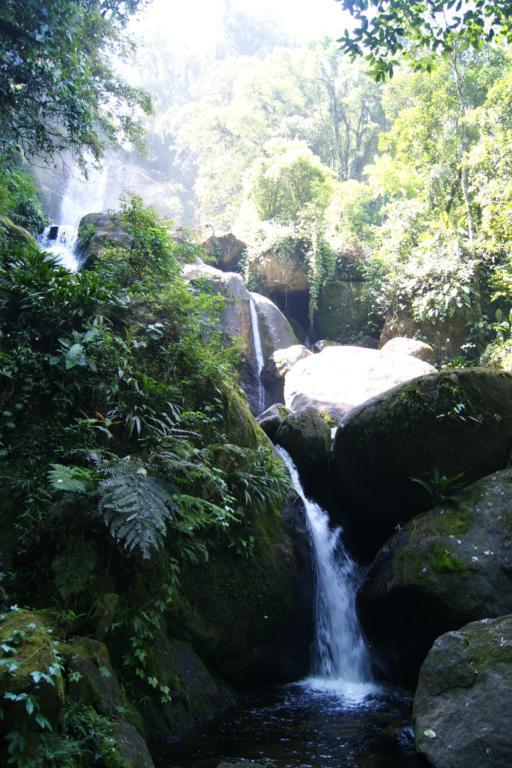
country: BR
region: Sao Paulo
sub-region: Bertioga
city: Bertioga
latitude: -23.7775
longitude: -46.2576
